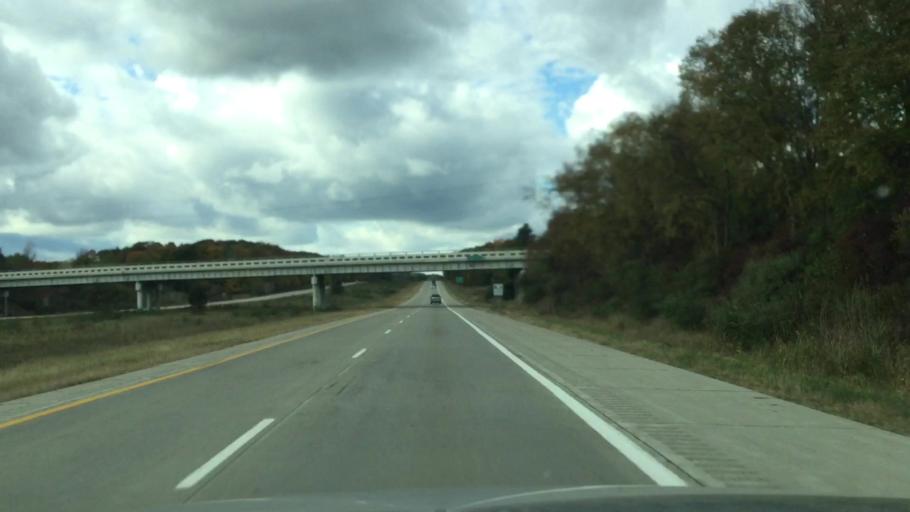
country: US
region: Michigan
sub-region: Lapeer County
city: Lapeer
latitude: 43.0222
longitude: -83.4085
